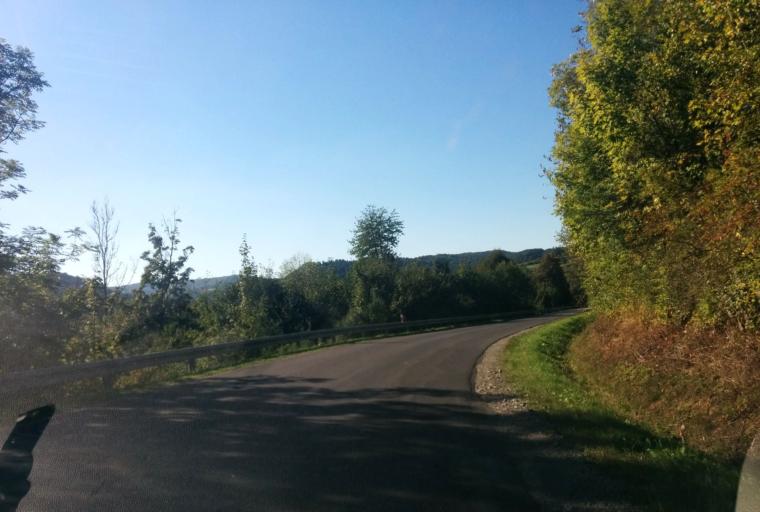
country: PL
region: Subcarpathian Voivodeship
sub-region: Powiat leski
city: Polanczyk
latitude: 49.3323
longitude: 22.4220
